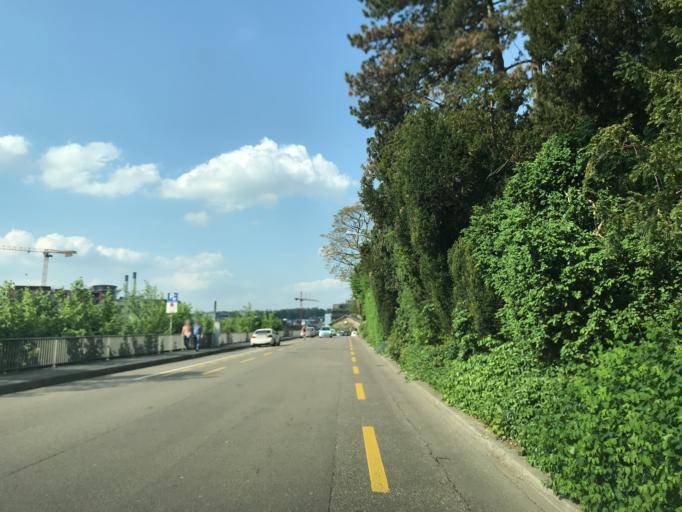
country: CH
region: Zurich
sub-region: Bezirk Winterthur
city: Stadt Winterthur (Kreis 1)
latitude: 47.4953
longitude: 8.7210
